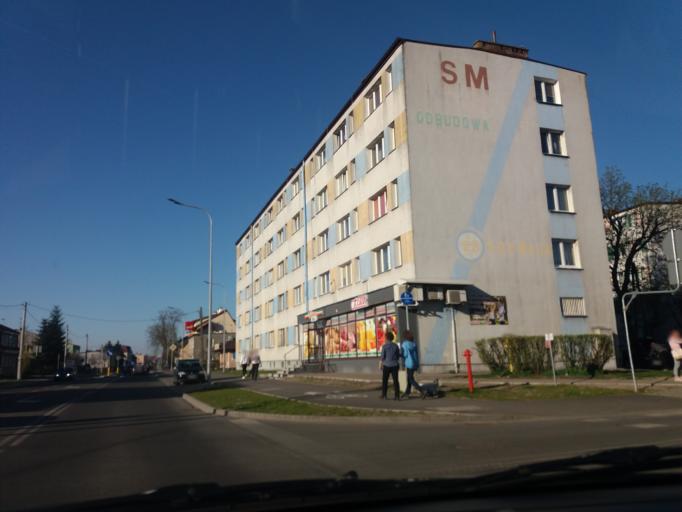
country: PL
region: Warmian-Masurian Voivodeship
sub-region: Powiat nidzicki
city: Nidzica
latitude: 53.3638
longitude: 20.4272
